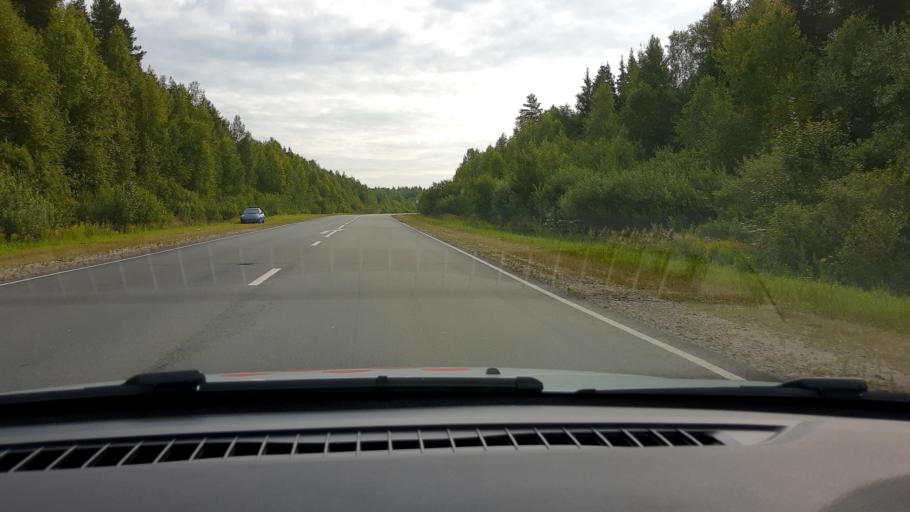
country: RU
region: Nizjnij Novgorod
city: Semenov
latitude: 56.8198
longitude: 44.4928
